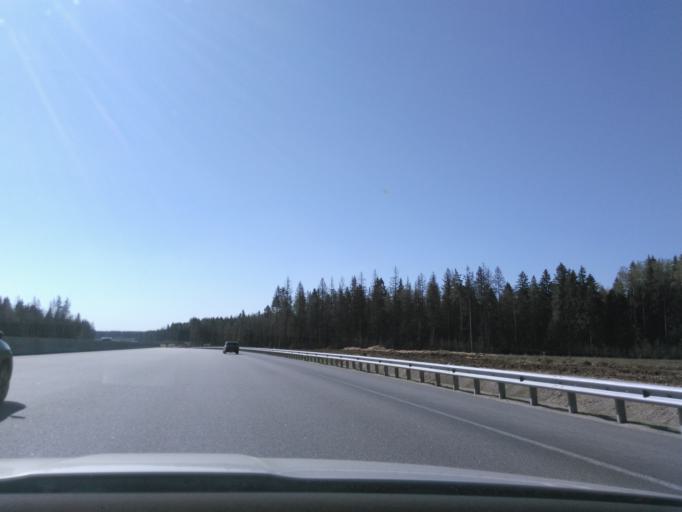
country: RU
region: Moskovskaya
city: Skhodnya
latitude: 55.9863
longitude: 37.3069
